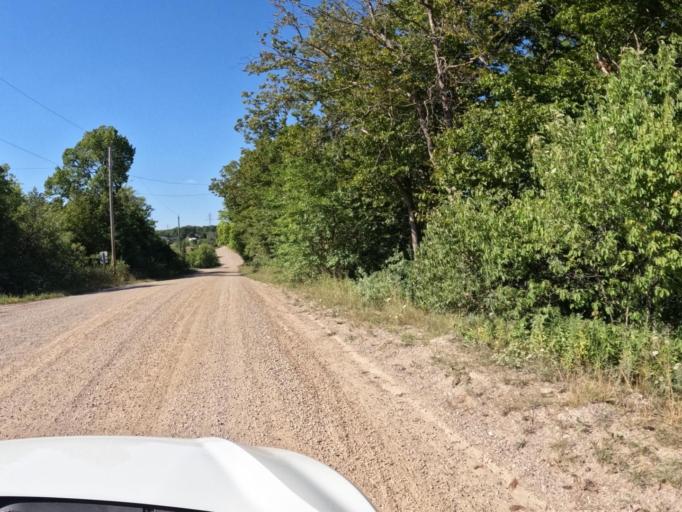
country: CA
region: Ontario
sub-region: Wellington County
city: Guelph
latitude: 43.4223
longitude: -80.1243
